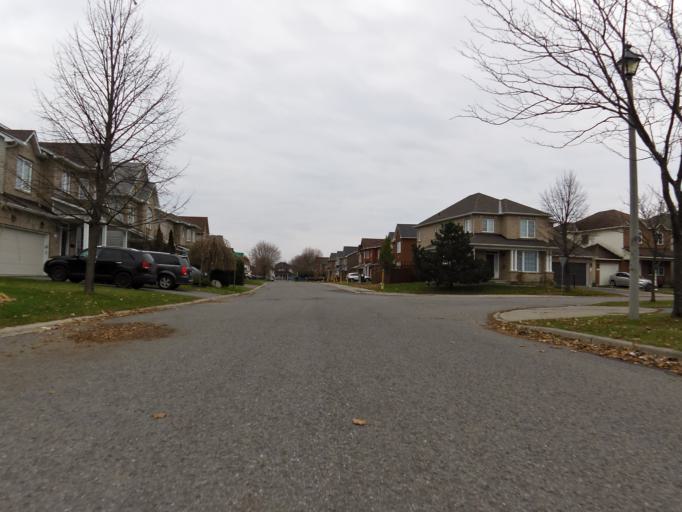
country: CA
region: Ontario
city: Bells Corners
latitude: 45.2811
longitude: -75.7112
